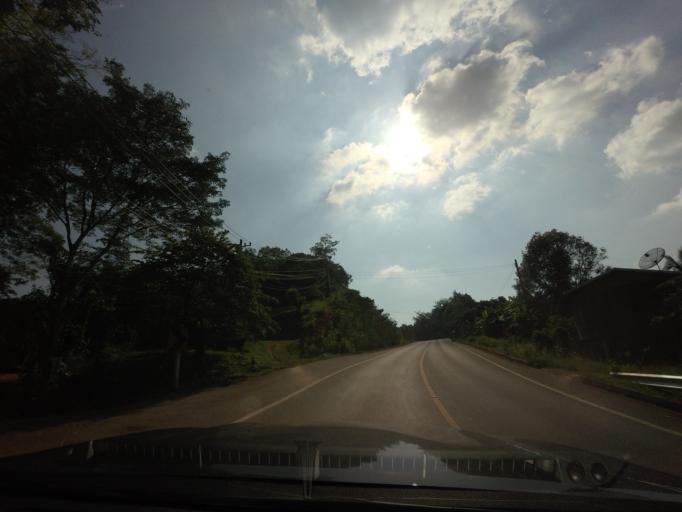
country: TH
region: Nan
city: Santi Suk
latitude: 18.9153
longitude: 100.8728
